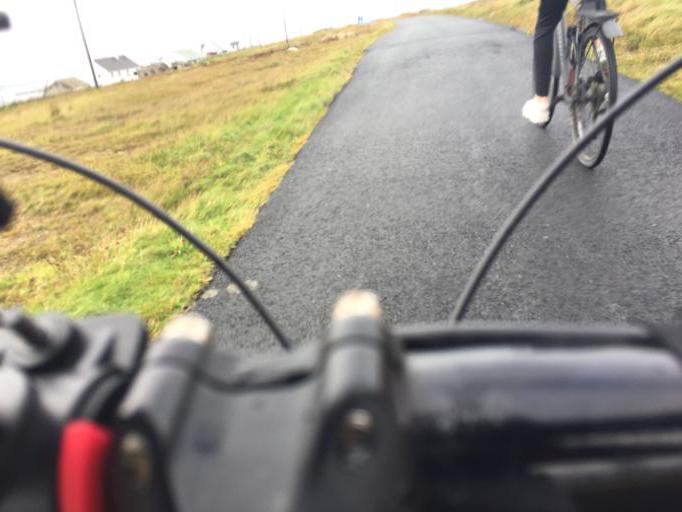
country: IE
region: Ulster
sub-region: County Donegal
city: Derrybeg
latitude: 55.2590
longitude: -8.2083
